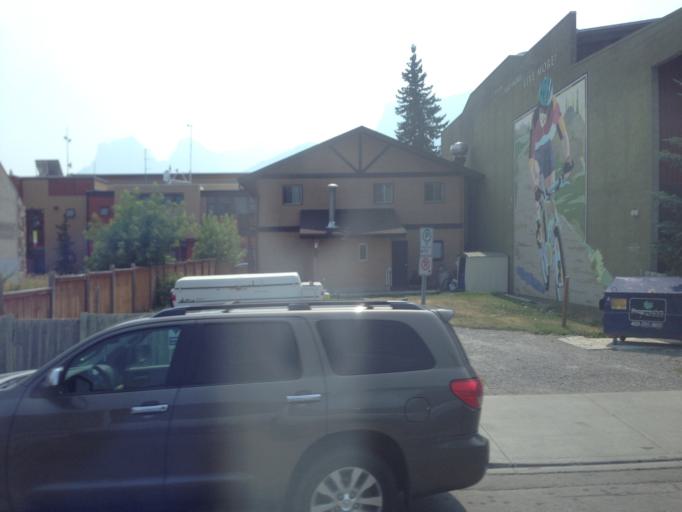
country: CA
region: Alberta
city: Canmore
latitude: 51.0904
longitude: -115.3600
